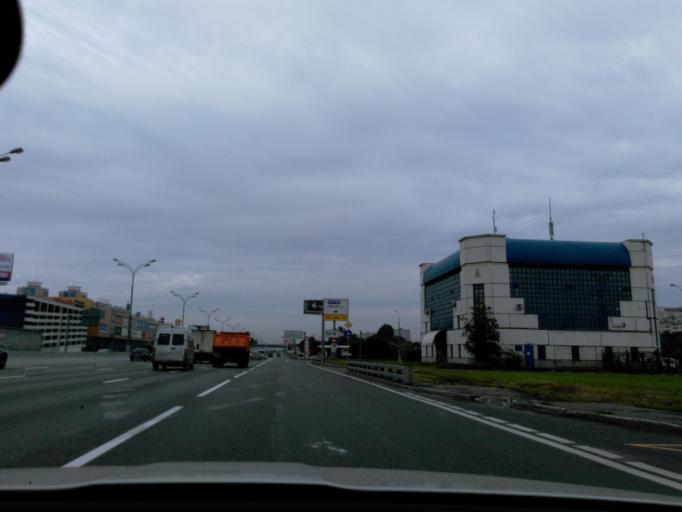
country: RU
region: Moscow
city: Ivanovskoye
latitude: 55.7682
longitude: 37.8428
